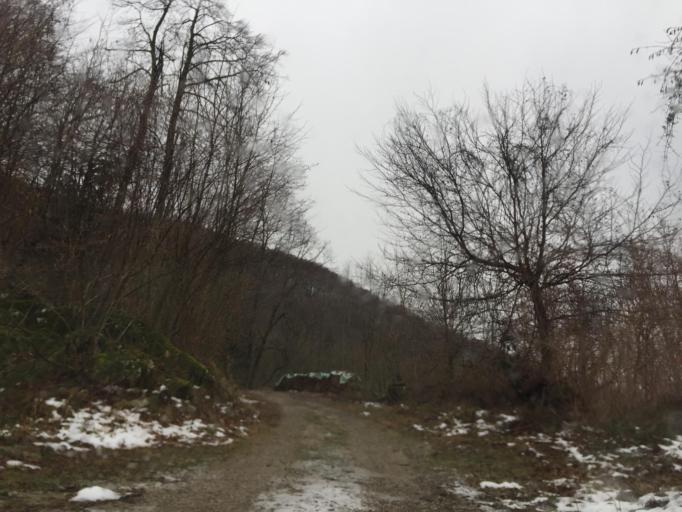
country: SI
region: Kanal
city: Kanal
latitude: 46.0728
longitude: 13.6753
